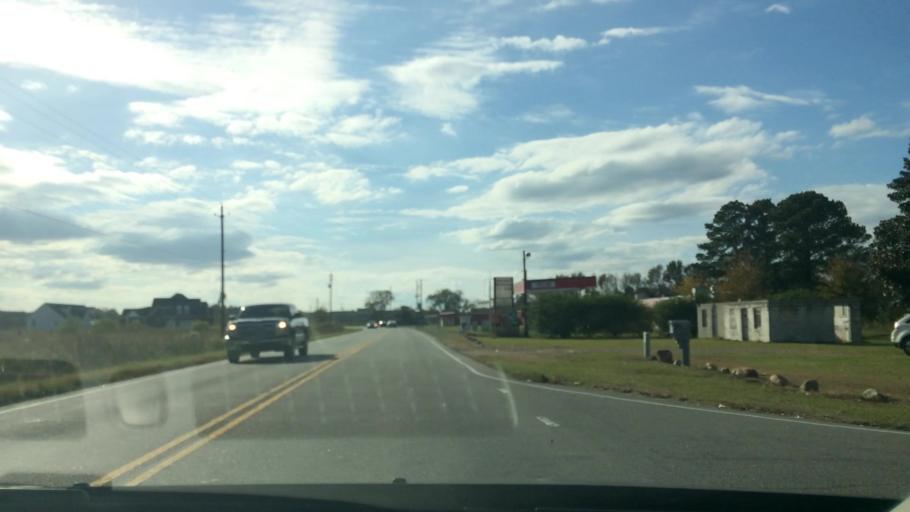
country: US
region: North Carolina
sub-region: Wayne County
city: Elroy
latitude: 35.4400
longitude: -77.8525
